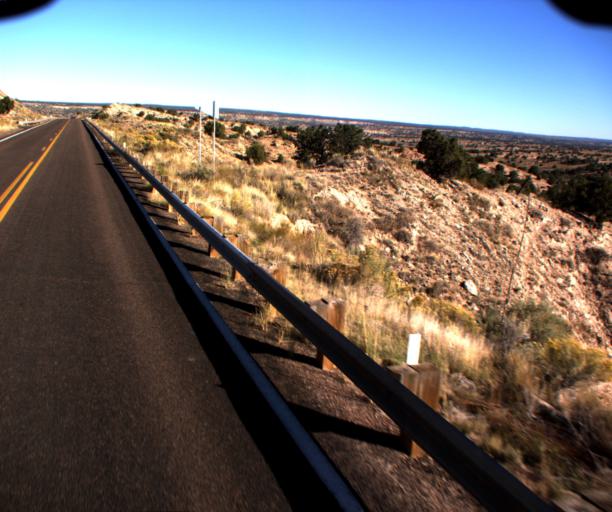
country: US
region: Arizona
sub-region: Navajo County
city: First Mesa
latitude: 35.7396
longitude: -110.1193
